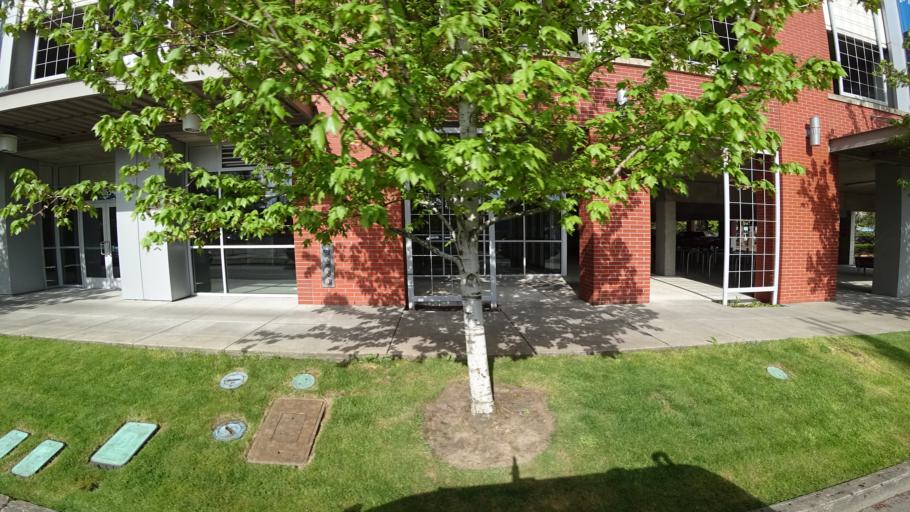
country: US
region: Oregon
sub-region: Washington County
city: Hillsboro
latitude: 45.5204
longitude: -122.9773
